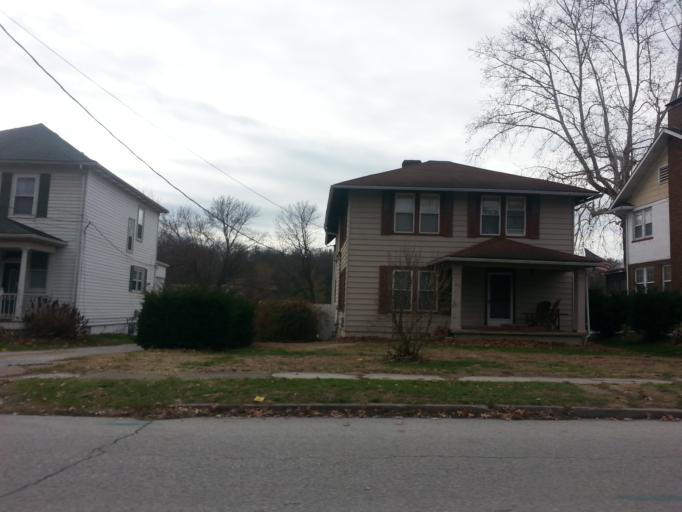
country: US
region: Missouri
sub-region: Marion County
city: Hannibal
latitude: 39.7115
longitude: -91.3901
